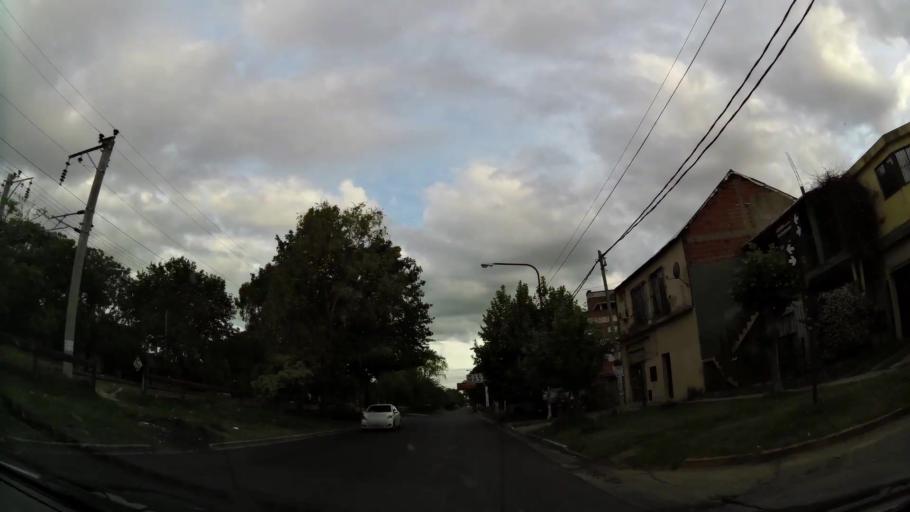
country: AR
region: Buenos Aires
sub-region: Partido de Quilmes
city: Quilmes
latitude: -34.7384
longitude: -58.2486
